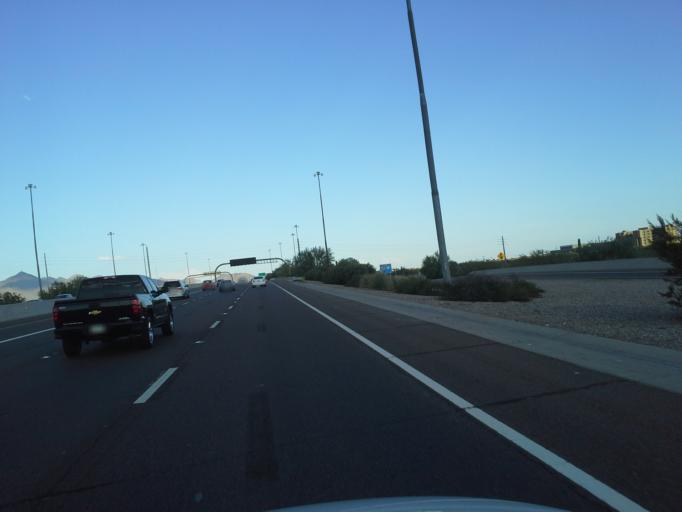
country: US
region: Arizona
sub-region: Maricopa County
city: Paradise Valley
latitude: 33.6692
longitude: -111.9633
